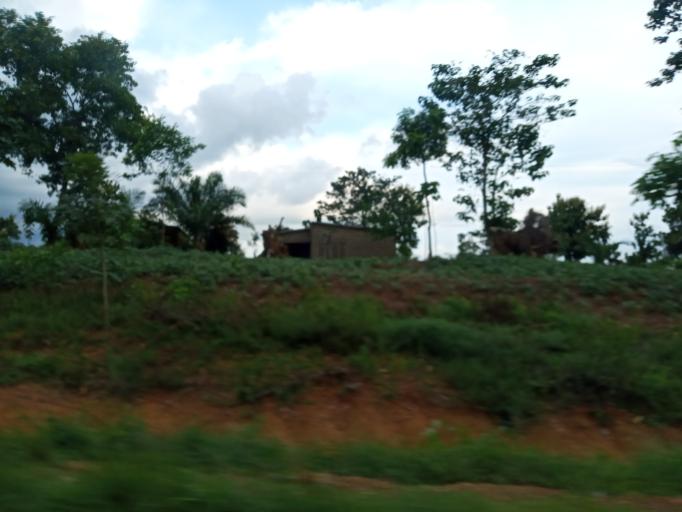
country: TG
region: Centrale
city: Sotouboua
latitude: 8.5828
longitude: 0.9863
